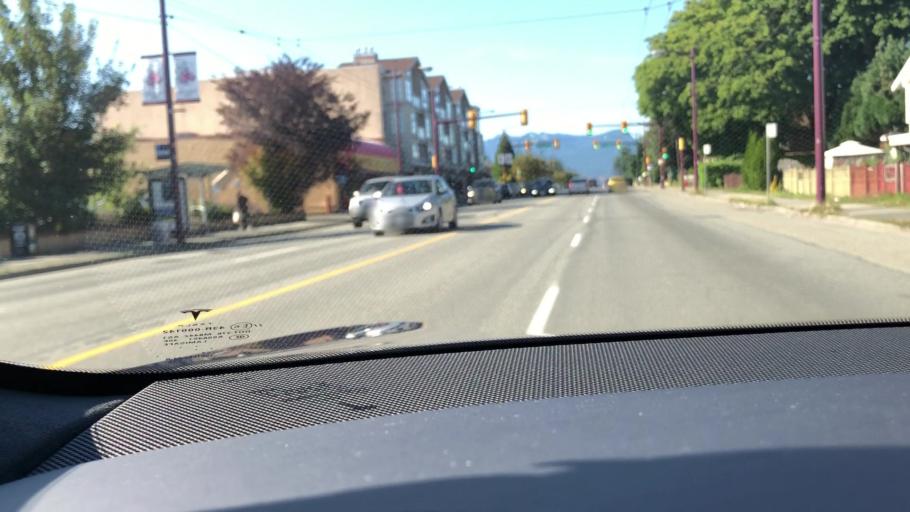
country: CA
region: British Columbia
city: Vancouver
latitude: 49.2264
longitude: -123.0657
